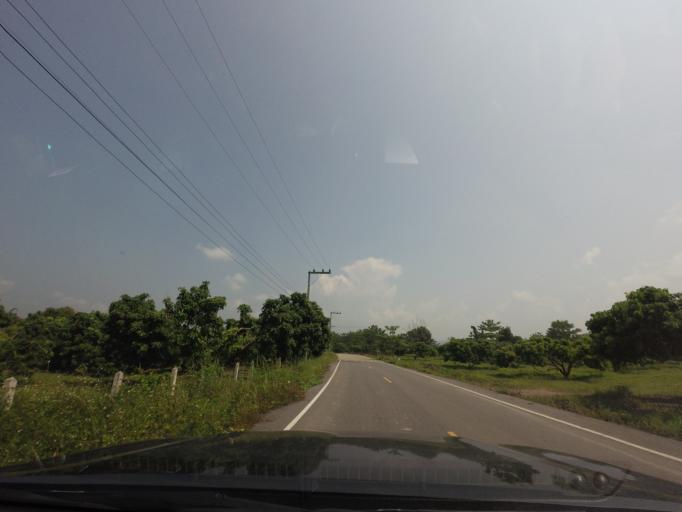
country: TH
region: Nan
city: Nan
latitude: 18.8565
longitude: 100.8054
